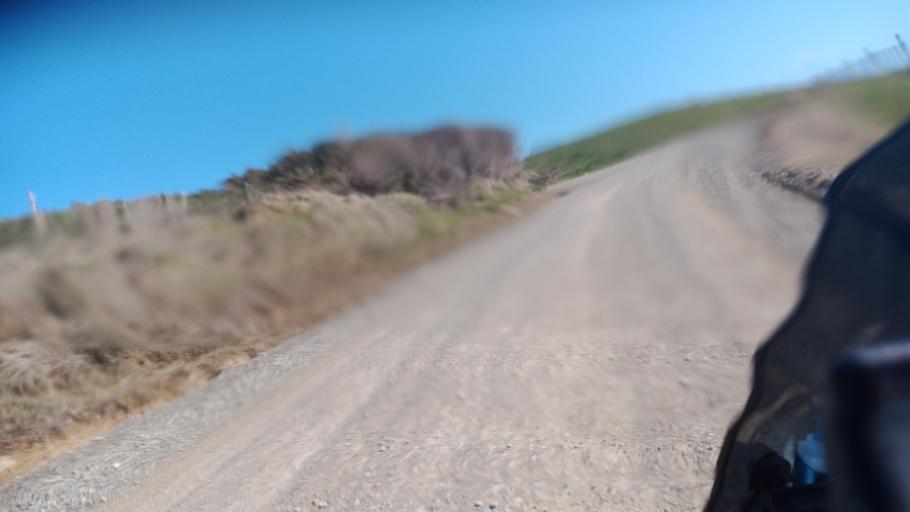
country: NZ
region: Gisborne
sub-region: Gisborne District
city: Gisborne
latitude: -39.1134
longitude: 177.9628
